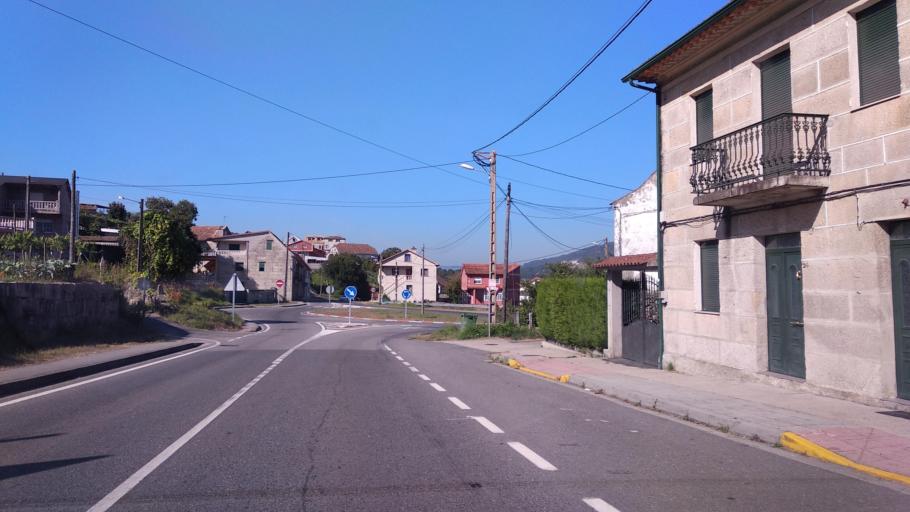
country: ES
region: Galicia
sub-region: Provincia de Pontevedra
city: Marin
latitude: 42.3463
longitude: -8.6437
